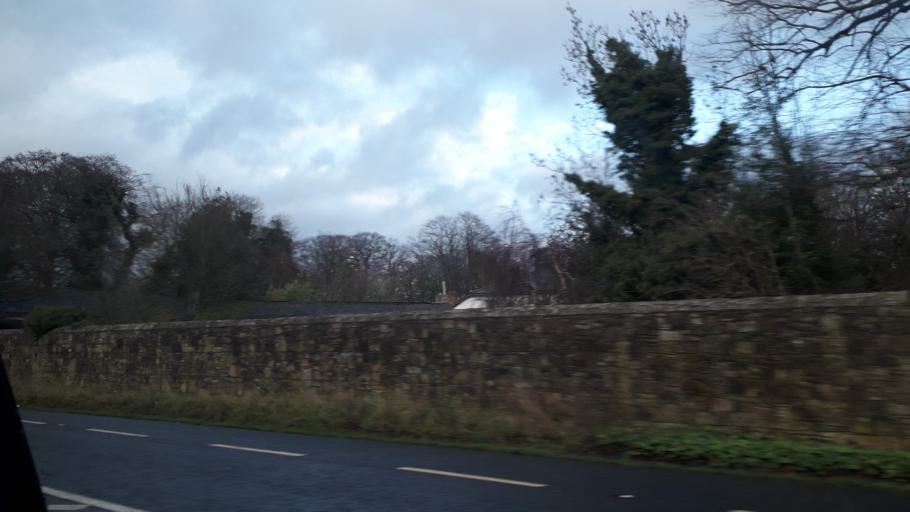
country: IE
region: Leinster
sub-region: Lu
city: Ardee
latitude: 53.8868
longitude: -6.5737
